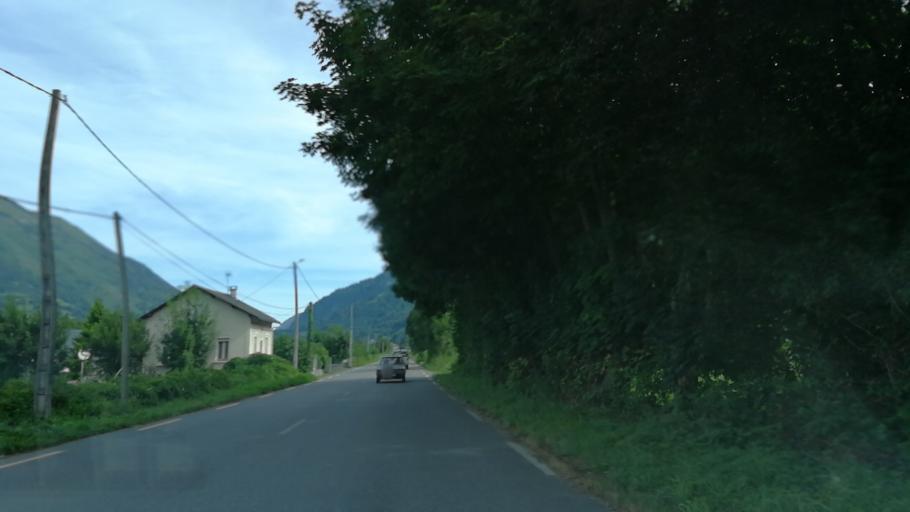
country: FR
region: Aquitaine
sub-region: Departement des Pyrenees-Atlantiques
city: Arette
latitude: 42.9862
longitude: -0.6042
